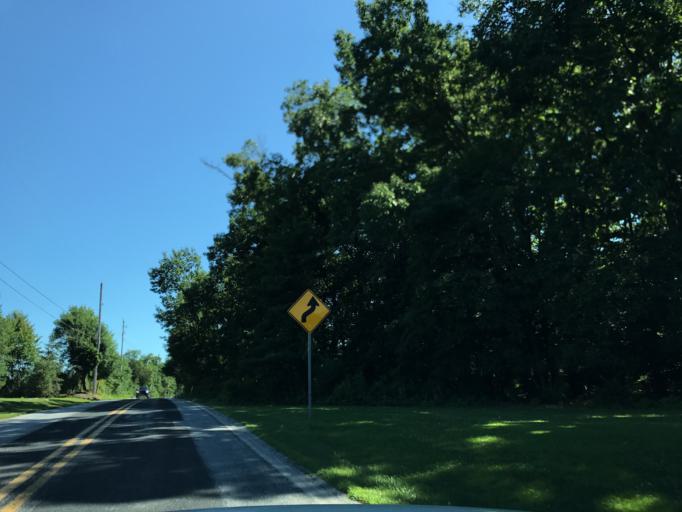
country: US
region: Pennsylvania
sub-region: York County
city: Pennville
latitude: 39.7735
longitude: -77.0062
